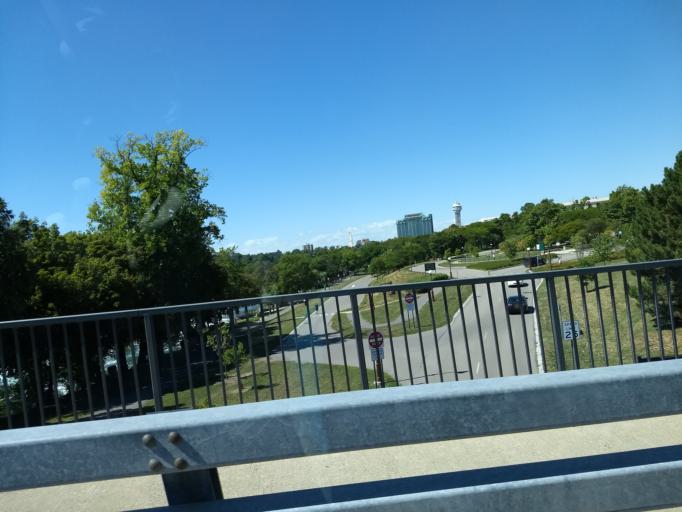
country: US
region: New York
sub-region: Niagara County
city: Niagara Falls
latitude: 43.0829
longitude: -79.0635
